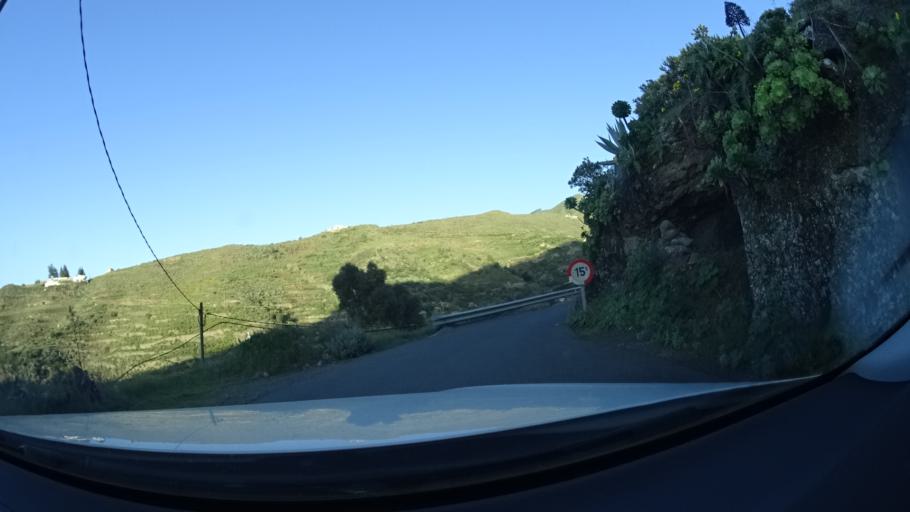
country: ES
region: Canary Islands
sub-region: Provincia de Las Palmas
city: Artenara
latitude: 28.0349
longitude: -15.6475
